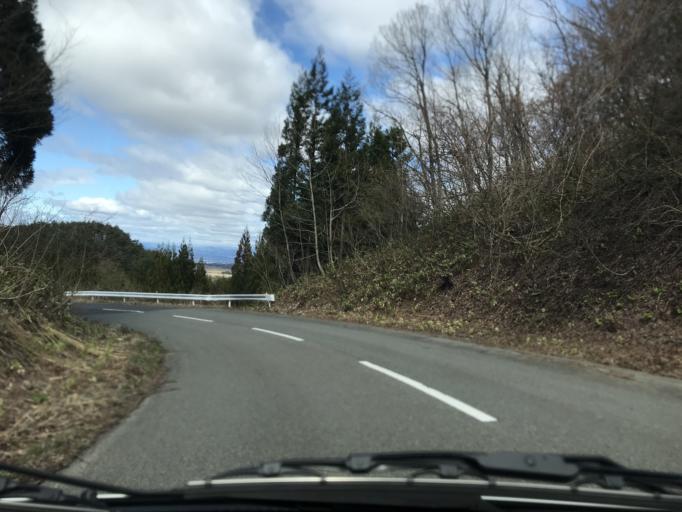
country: JP
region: Iwate
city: Mizusawa
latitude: 39.0673
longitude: 140.9822
